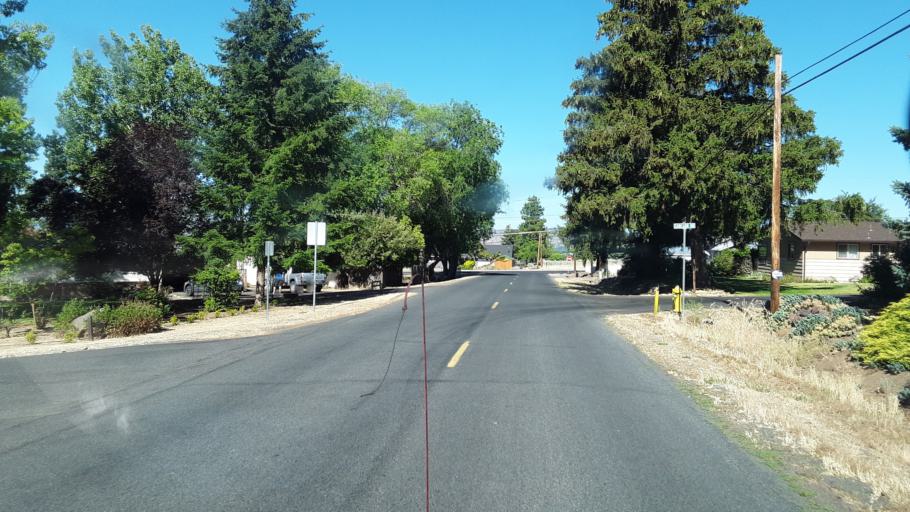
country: US
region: Oregon
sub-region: Klamath County
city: Altamont
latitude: 42.2175
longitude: -121.7115
